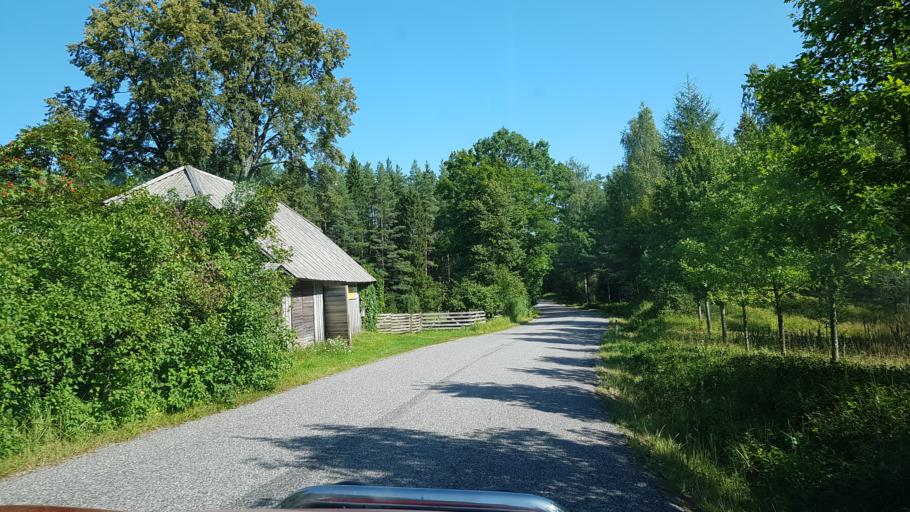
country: EE
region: Vorumaa
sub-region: Voru linn
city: Voru
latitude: 57.7151
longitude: 27.1960
